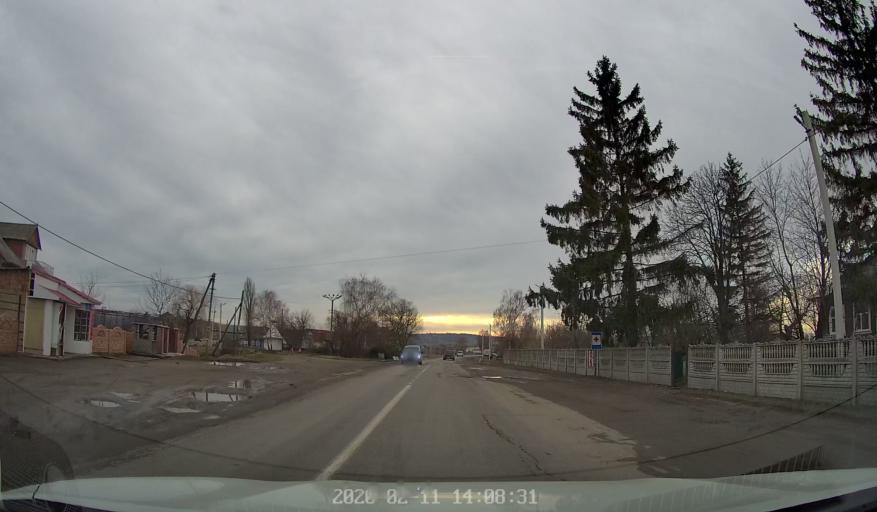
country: RO
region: Botosani
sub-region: Comuna Darabani
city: Bajura
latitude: 48.2364
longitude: 26.5464
